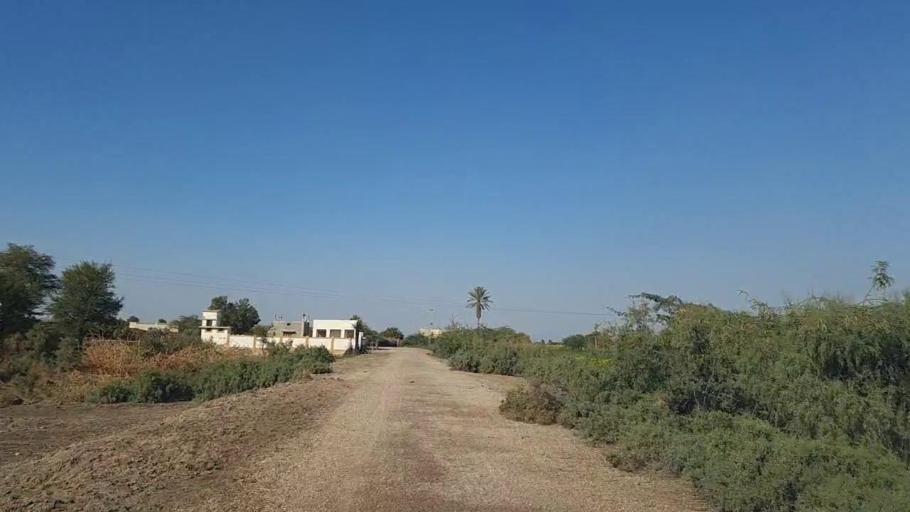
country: PK
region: Sindh
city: Shahpur Chakar
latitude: 26.2215
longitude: 68.6348
